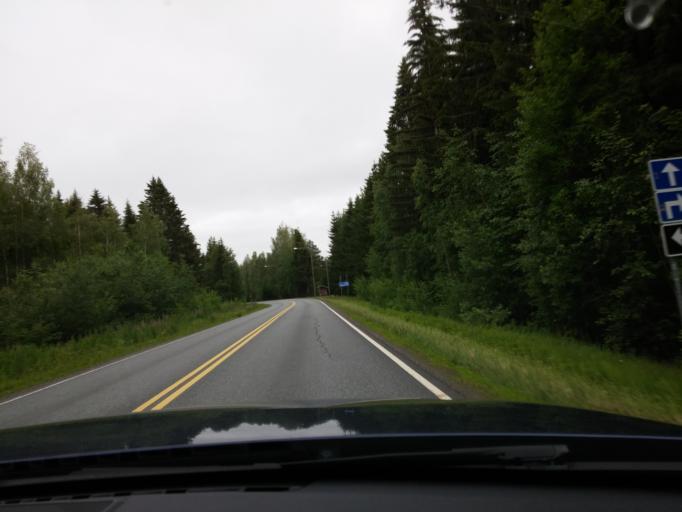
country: FI
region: Central Finland
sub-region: Joutsa
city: Joutsa
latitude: 61.8131
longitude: 25.9365
